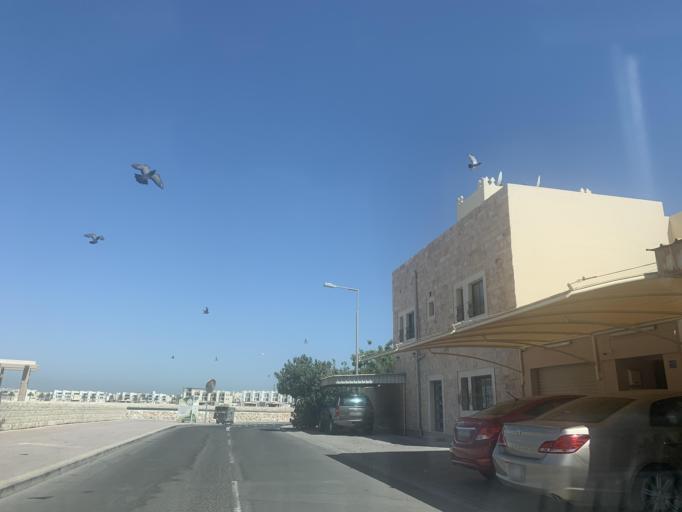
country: BH
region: Manama
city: Jidd Hafs
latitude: 26.2169
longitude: 50.4463
